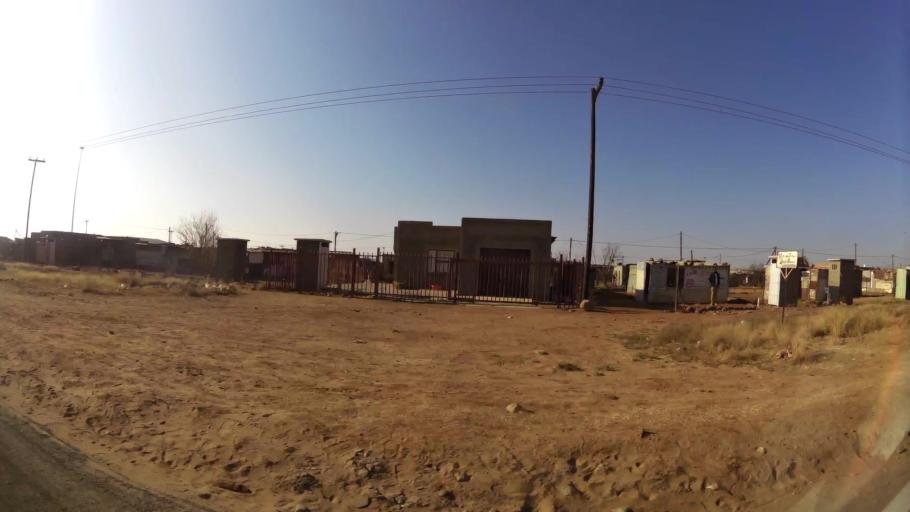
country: ZA
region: Orange Free State
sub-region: Mangaung Metropolitan Municipality
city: Bloemfontein
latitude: -29.2037
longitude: 26.2521
